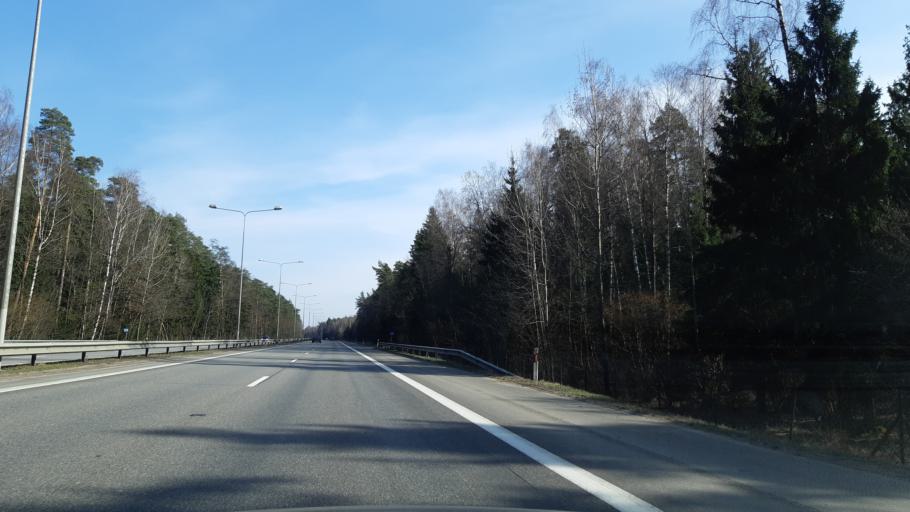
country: LT
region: Kauno apskritis
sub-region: Kauno rajonas
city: Karmelava
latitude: 54.8928
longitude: 24.1583
